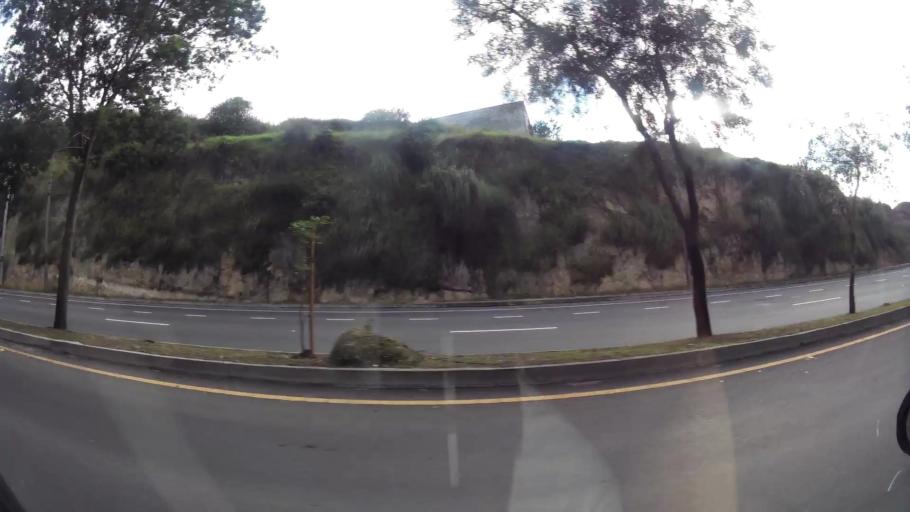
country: EC
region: Pichincha
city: Quito
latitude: -0.2330
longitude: -78.4932
